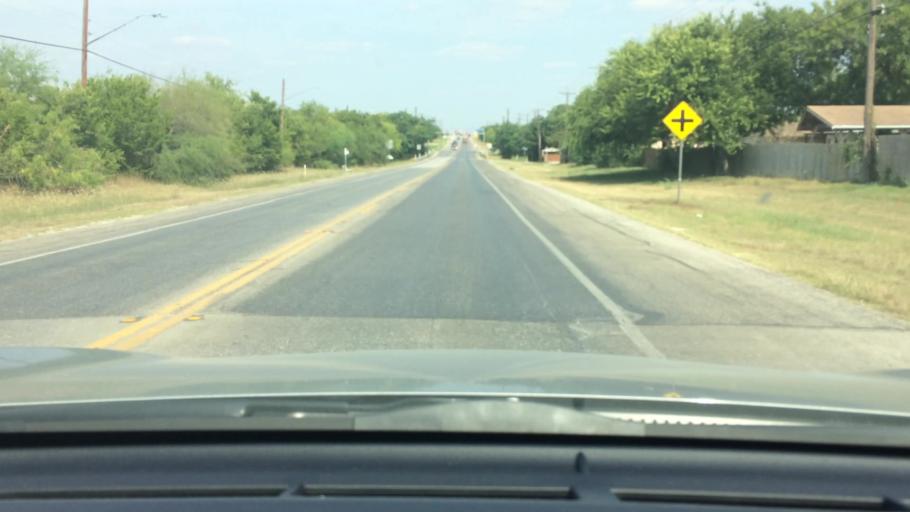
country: US
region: Texas
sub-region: Bexar County
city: China Grove
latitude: 29.3273
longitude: -98.4357
